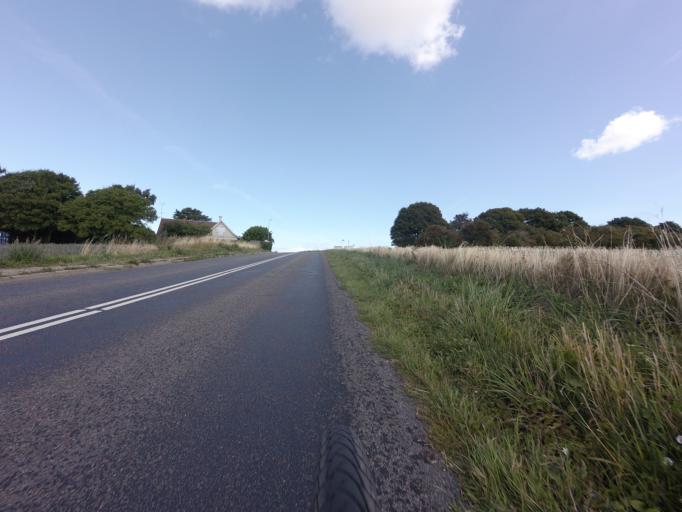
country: DK
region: Zealand
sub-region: Vordingborg Kommune
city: Stege
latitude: 54.9700
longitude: 12.4817
